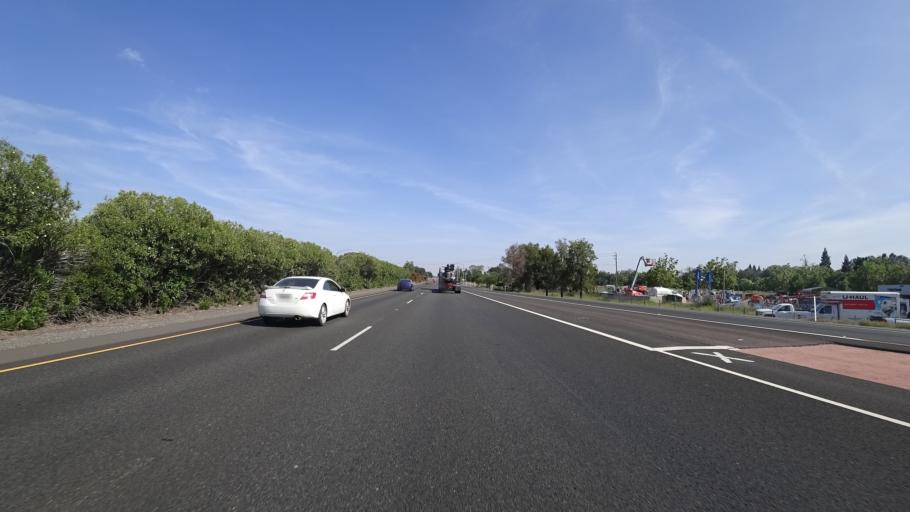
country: US
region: California
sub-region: Butte County
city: Chico
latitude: 39.7127
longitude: -121.7990
